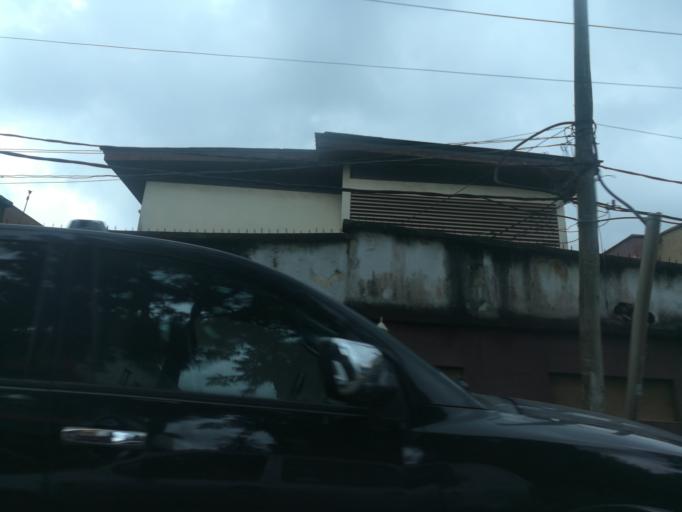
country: NG
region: Lagos
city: Ikeja
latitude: 6.6178
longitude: 3.3485
